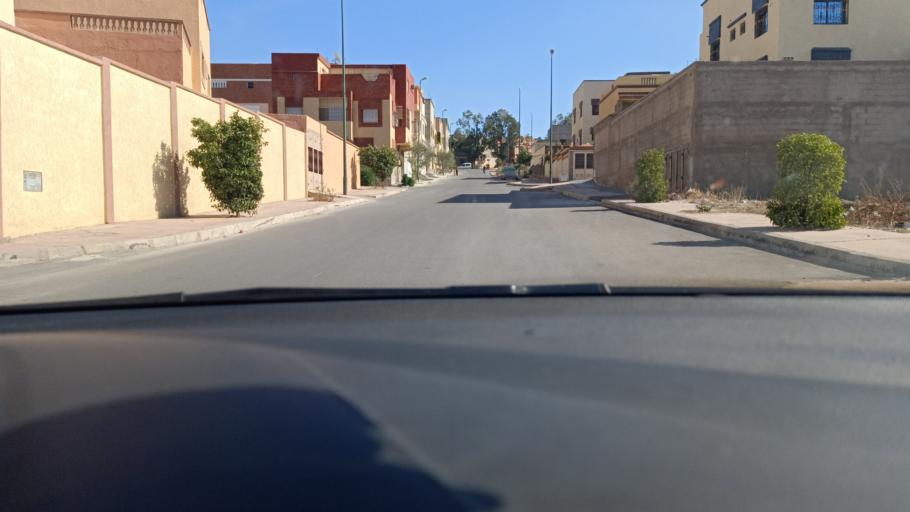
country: MA
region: Doukkala-Abda
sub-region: Safi
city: Youssoufia
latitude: 32.2418
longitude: -8.5316
